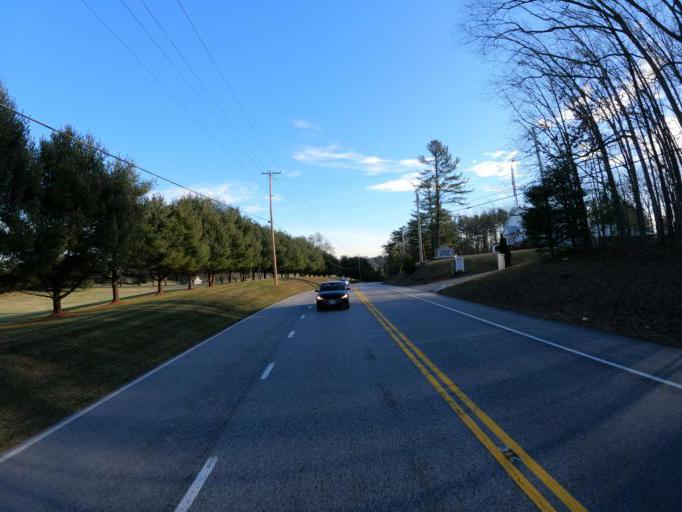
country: US
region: Maryland
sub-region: Montgomery County
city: Olney
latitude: 39.2652
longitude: -77.0473
